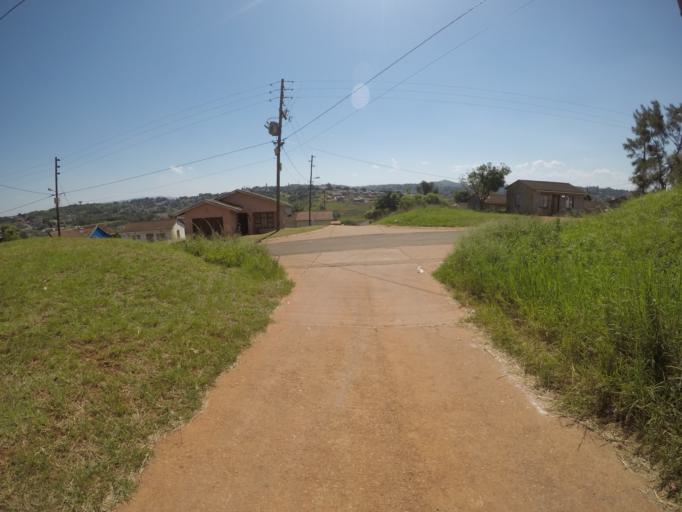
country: ZA
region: KwaZulu-Natal
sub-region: uThungulu District Municipality
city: Empangeni
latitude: -28.7698
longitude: 31.8765
